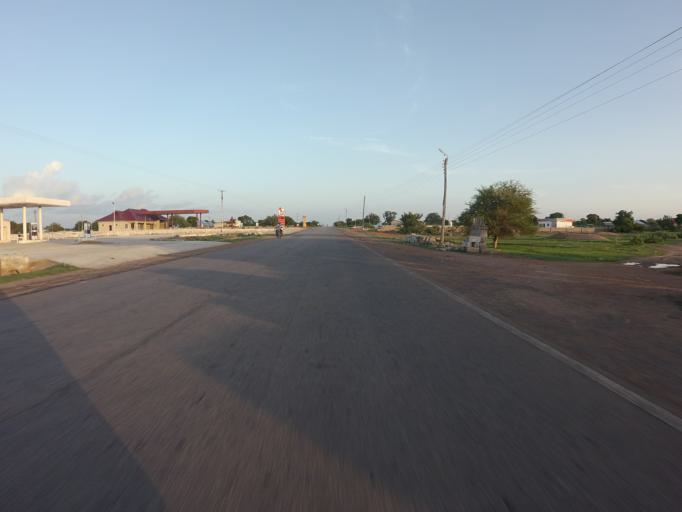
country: GH
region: Upper East
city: Navrongo
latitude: 10.9524
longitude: -1.0960
